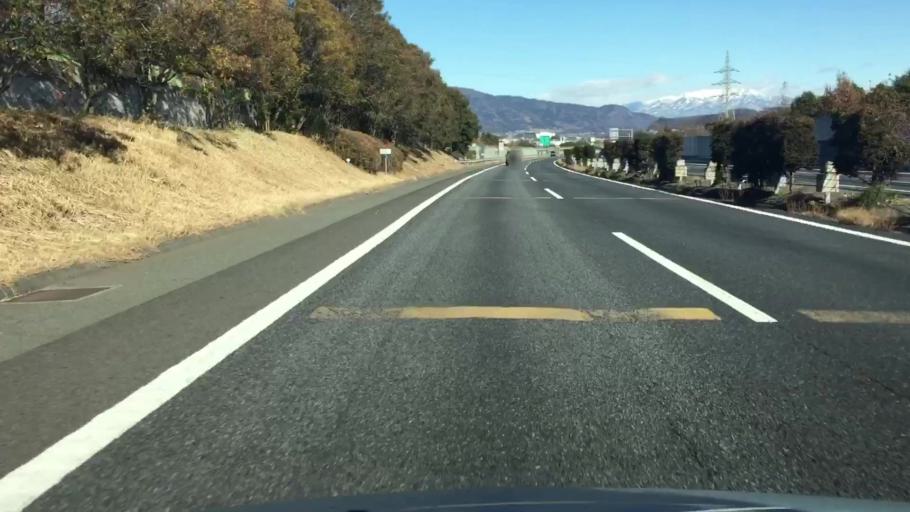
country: JP
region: Gunma
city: Shibukawa
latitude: 36.4660
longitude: 139.0115
